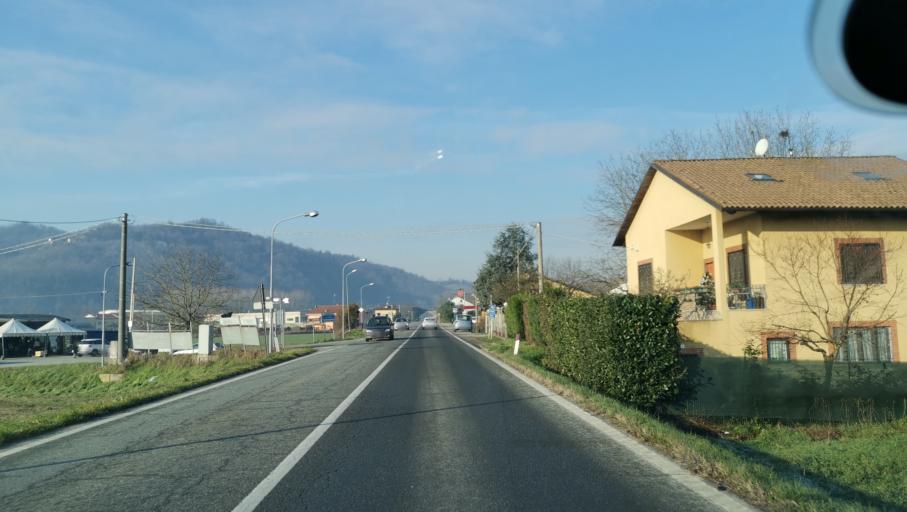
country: IT
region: Piedmont
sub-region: Provincia di Torino
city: San Sebastiano da Po
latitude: 45.1709
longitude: 7.9388
